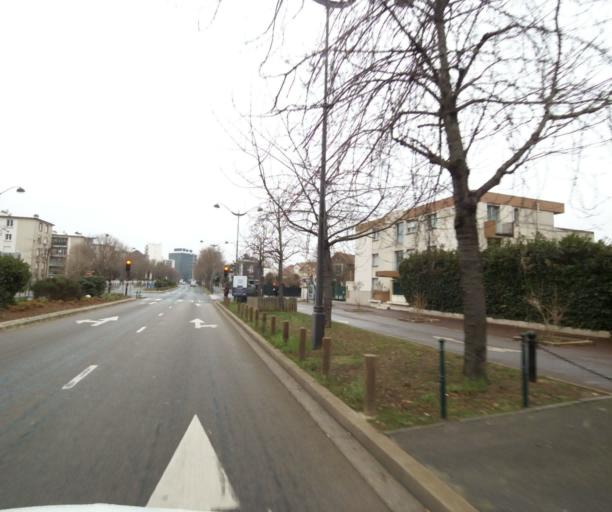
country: FR
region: Ile-de-France
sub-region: Departement des Hauts-de-Seine
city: Rueil-Malmaison
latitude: 48.8873
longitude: 2.1802
